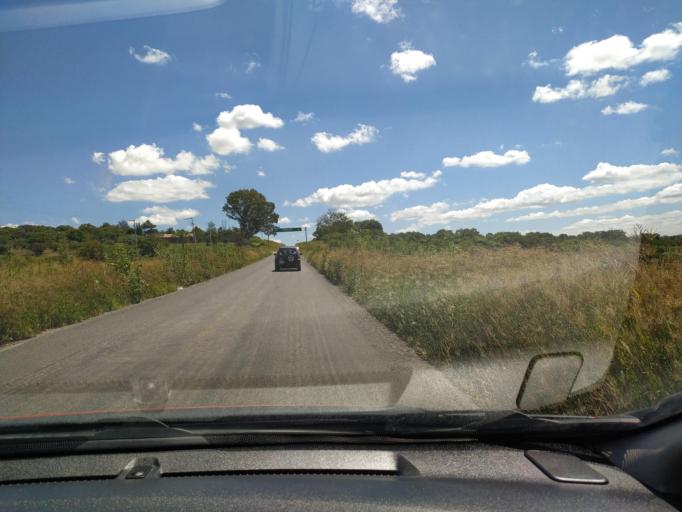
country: MX
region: Jalisco
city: San Julian
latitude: 21.0047
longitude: -102.1150
